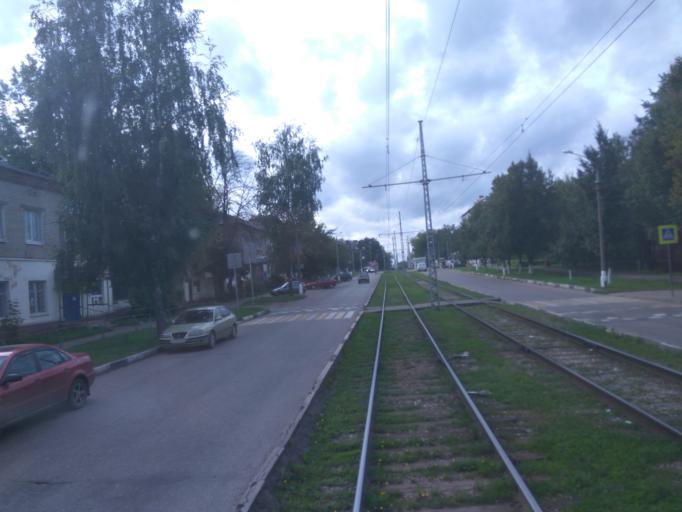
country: RU
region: Moskovskaya
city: Kolomna
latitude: 55.0799
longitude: 38.7653
